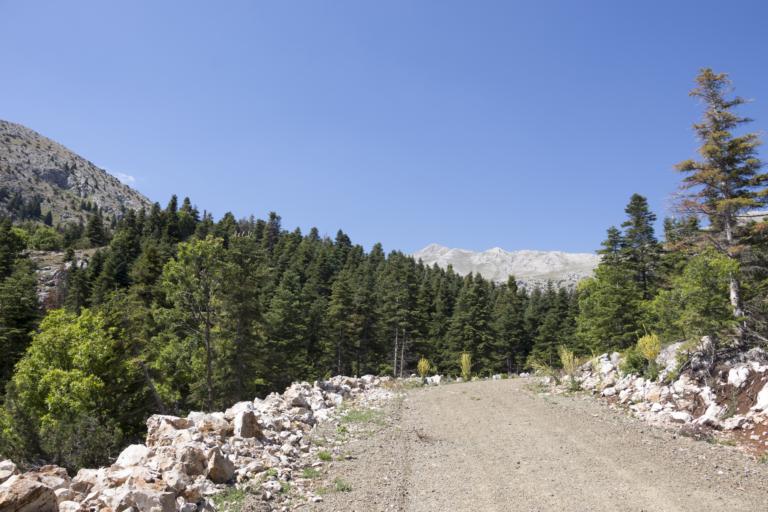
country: TR
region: Kayseri
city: Toklar
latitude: 38.3355
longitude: 36.0610
